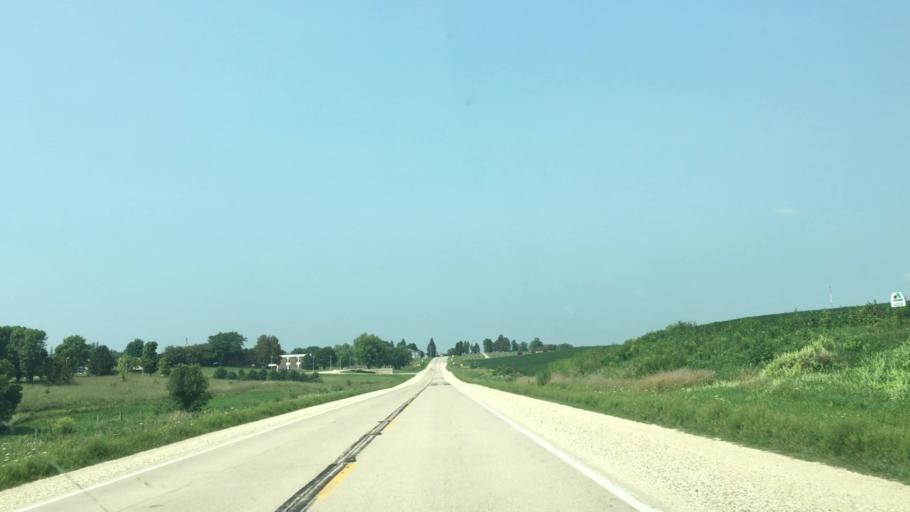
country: US
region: Iowa
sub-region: Winneshiek County
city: Decorah
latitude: 43.1703
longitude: -91.8644
